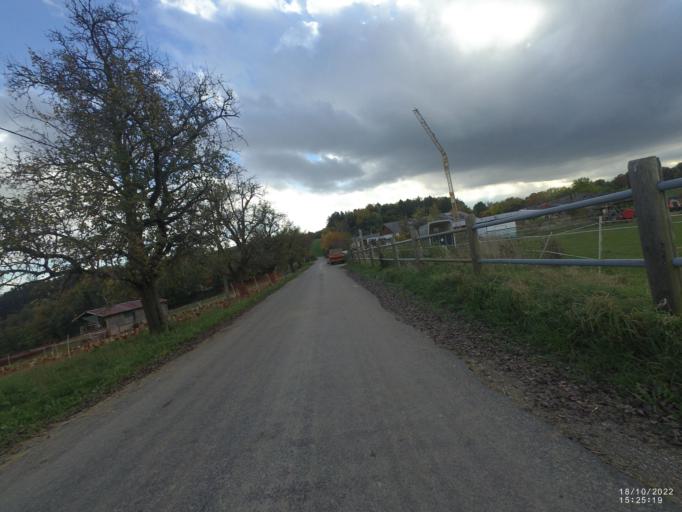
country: DE
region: Baden-Wuerttemberg
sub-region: Regierungsbezirk Stuttgart
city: Ottenbach
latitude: 48.7128
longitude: 9.7727
